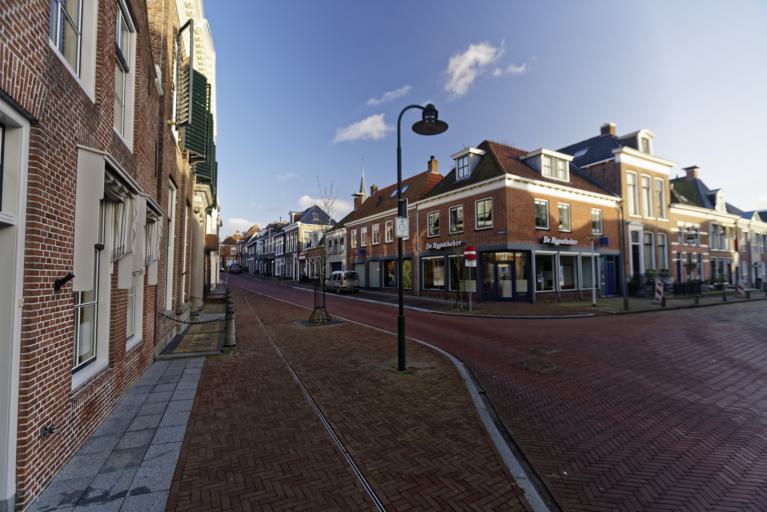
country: NL
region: Friesland
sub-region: Gemeente Dongeradeel
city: Dokkum
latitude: 53.3266
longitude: 5.9960
